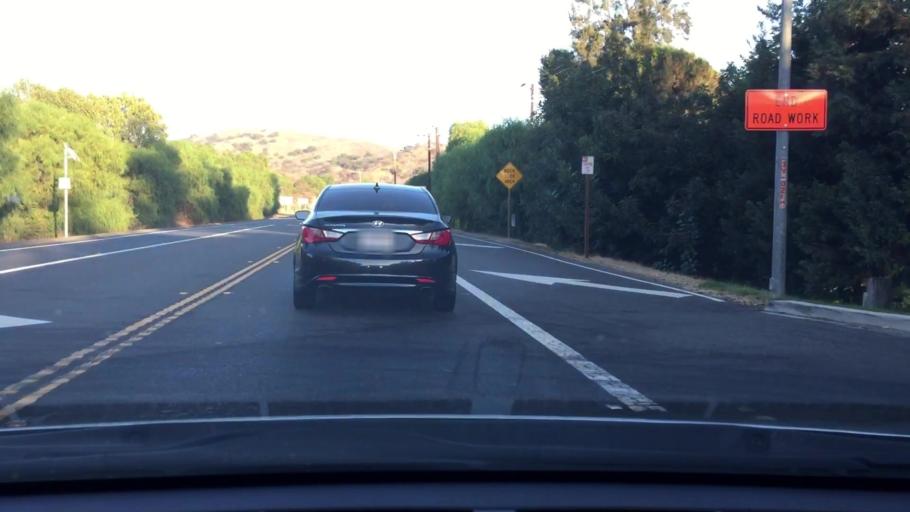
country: US
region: California
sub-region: Orange County
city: Yorba Linda
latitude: 33.9216
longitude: -117.8300
